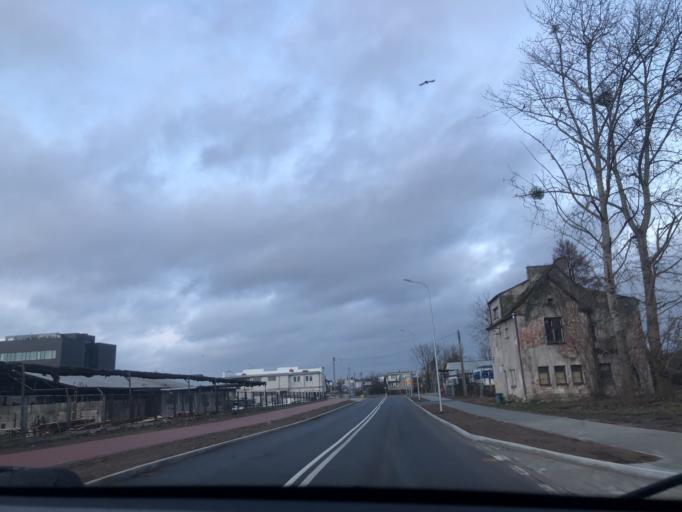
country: PL
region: Podlasie
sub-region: Lomza
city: Lomza
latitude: 53.1733
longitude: 22.0633
